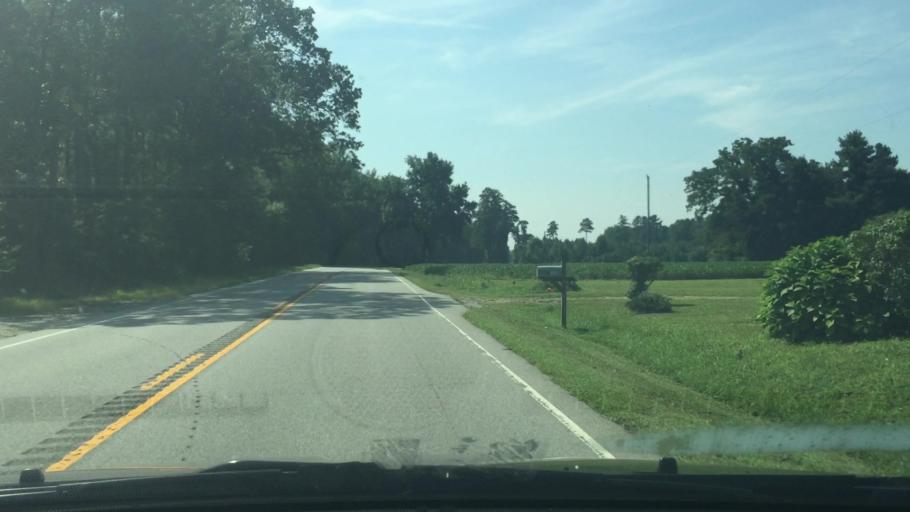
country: US
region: Virginia
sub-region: Sussex County
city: Sussex
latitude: 36.8577
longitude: -77.1361
